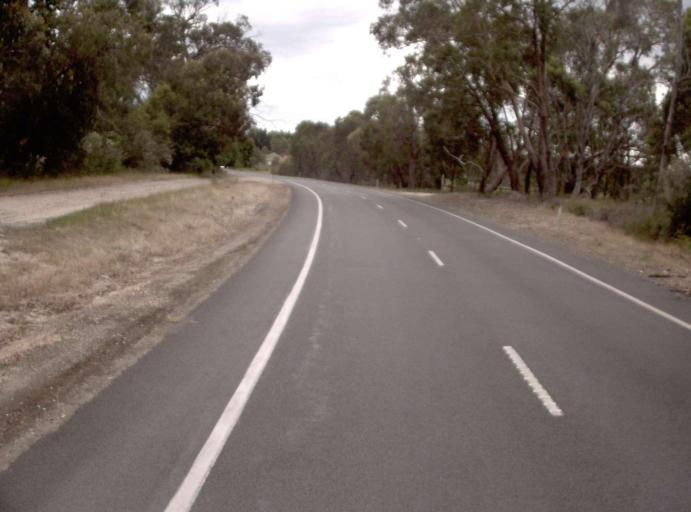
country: AU
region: Victoria
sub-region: Wellington
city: Sale
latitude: -38.2466
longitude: 147.0558
